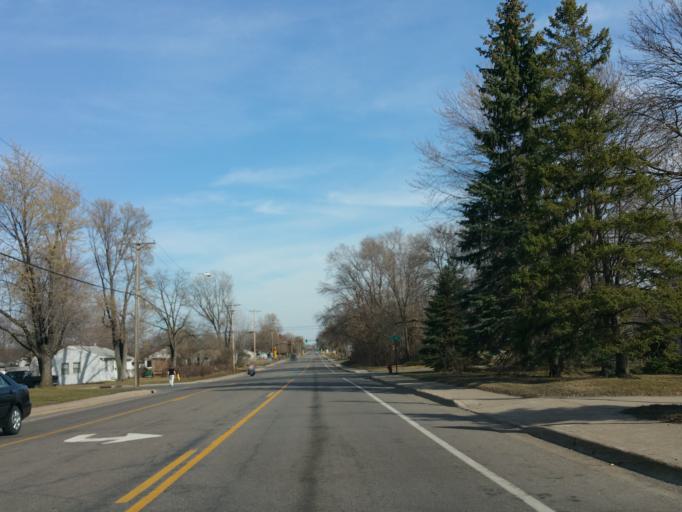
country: US
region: Minnesota
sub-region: Hennepin County
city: Bloomington
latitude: 44.8480
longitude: -93.2615
